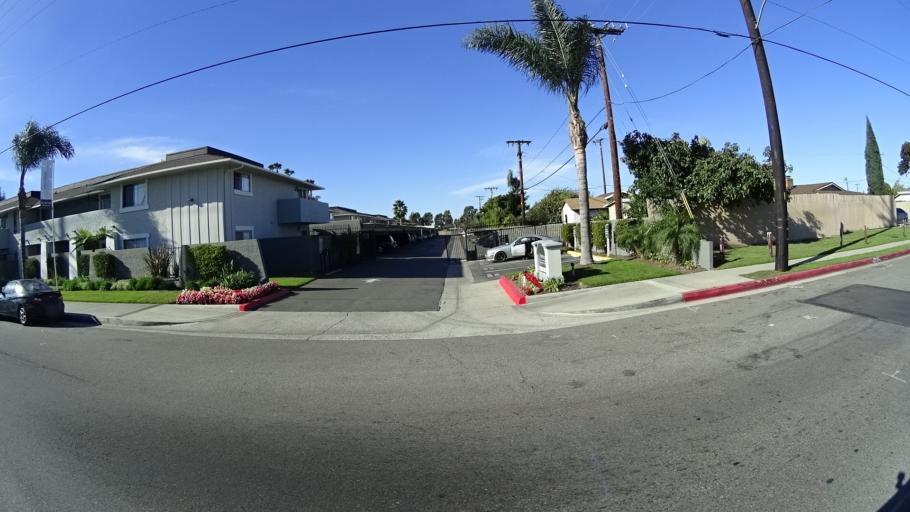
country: US
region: California
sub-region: Orange County
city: Westminster
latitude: 33.7751
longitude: -117.9840
